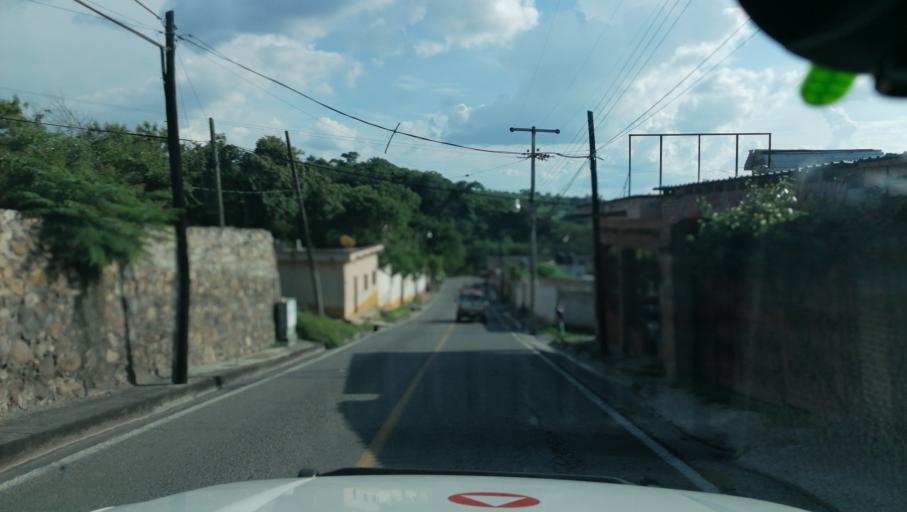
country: MX
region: Morelos
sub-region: Tepalcingo
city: Zacapalco
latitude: 18.6393
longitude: -99.0056
